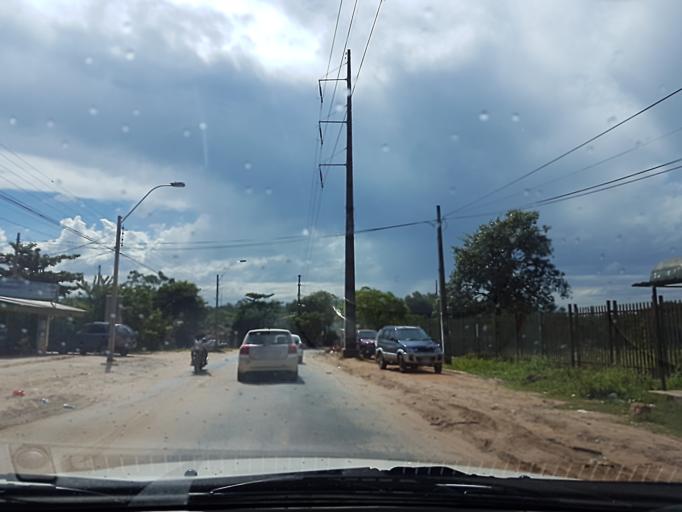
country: PY
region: Central
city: Colonia Mariano Roque Alonso
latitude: -25.2406
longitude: -57.5797
